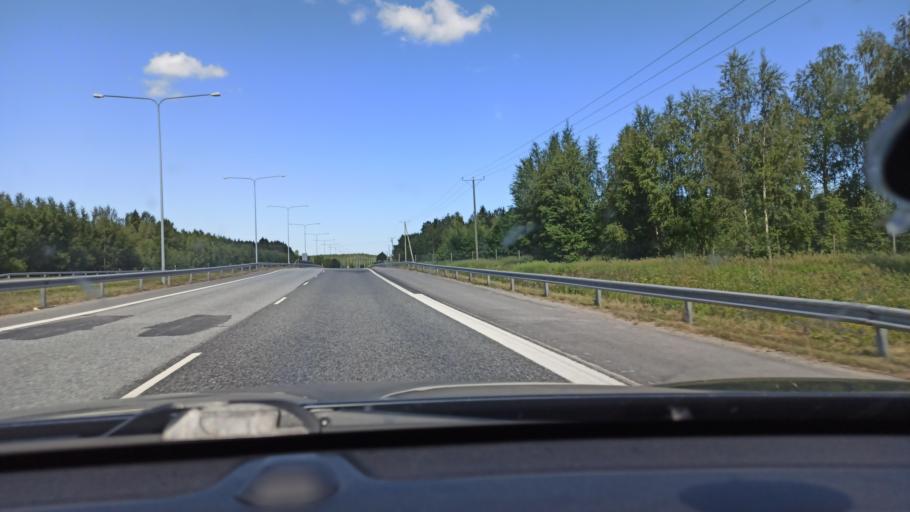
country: FI
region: Ostrobothnia
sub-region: Vaasa
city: Ristinummi
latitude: 63.0393
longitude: 21.7335
